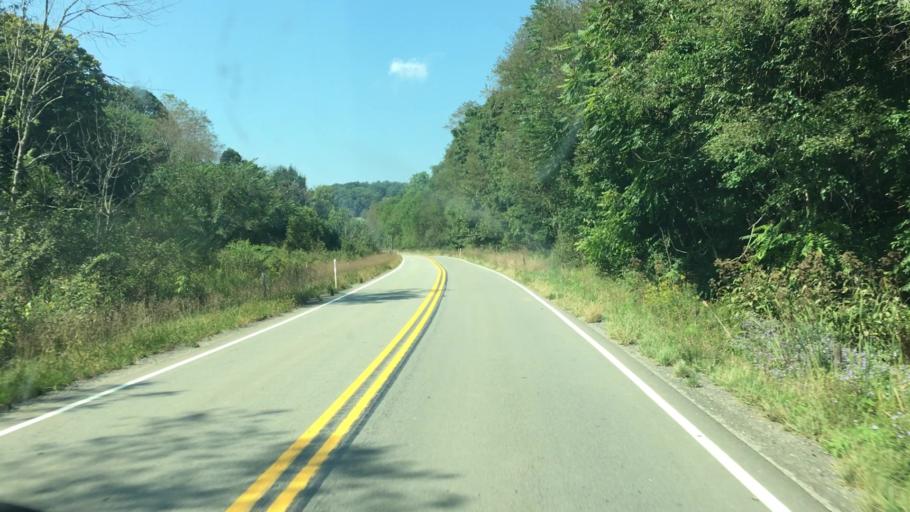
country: US
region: Pennsylvania
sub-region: Greene County
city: Waynesburg
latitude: 39.9743
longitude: -80.3255
